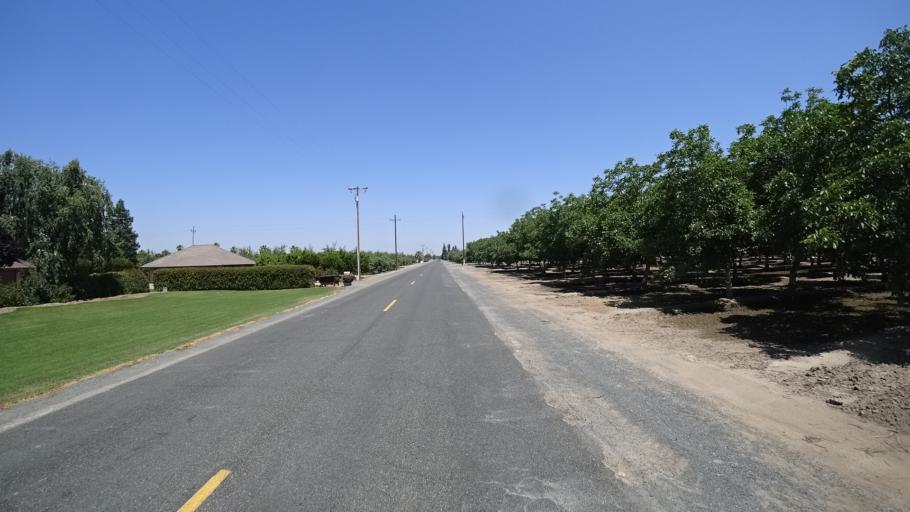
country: US
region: California
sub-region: Kings County
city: Lucerne
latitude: 36.4036
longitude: -119.6730
